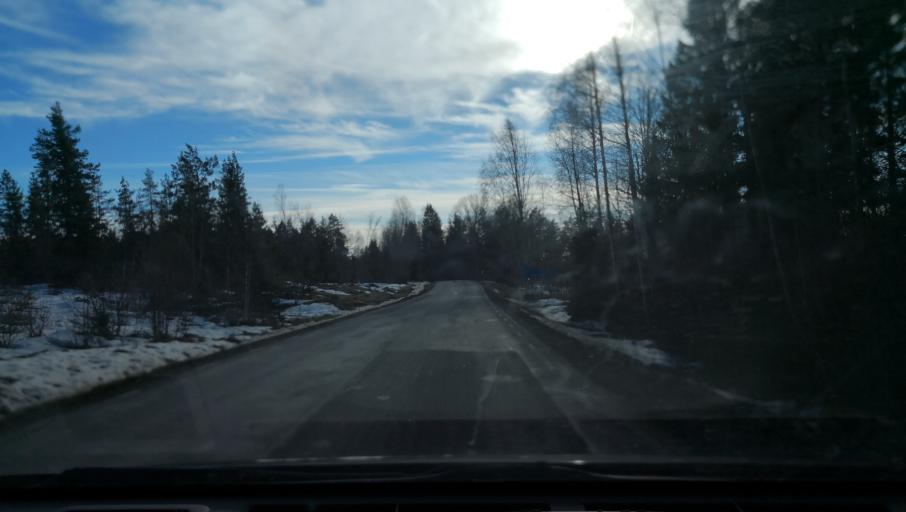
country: SE
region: Uppsala
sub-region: Osthammars Kommun
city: Osterbybruk
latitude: 60.2585
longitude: 17.9485
